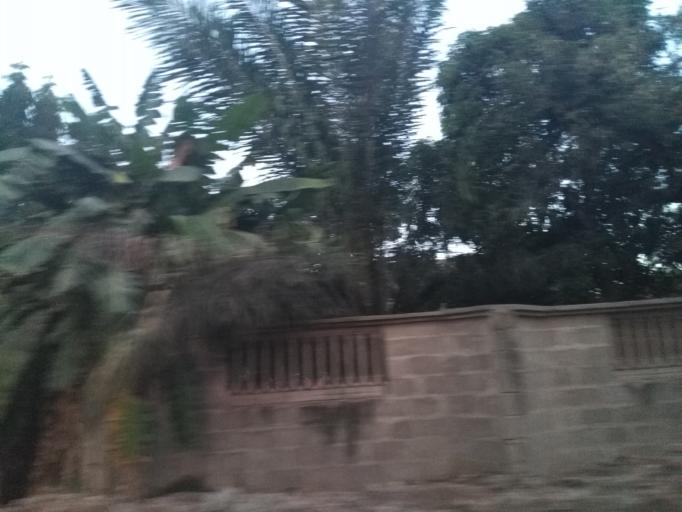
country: TZ
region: Dar es Salaam
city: Magomeni
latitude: -6.7661
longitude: 39.2779
